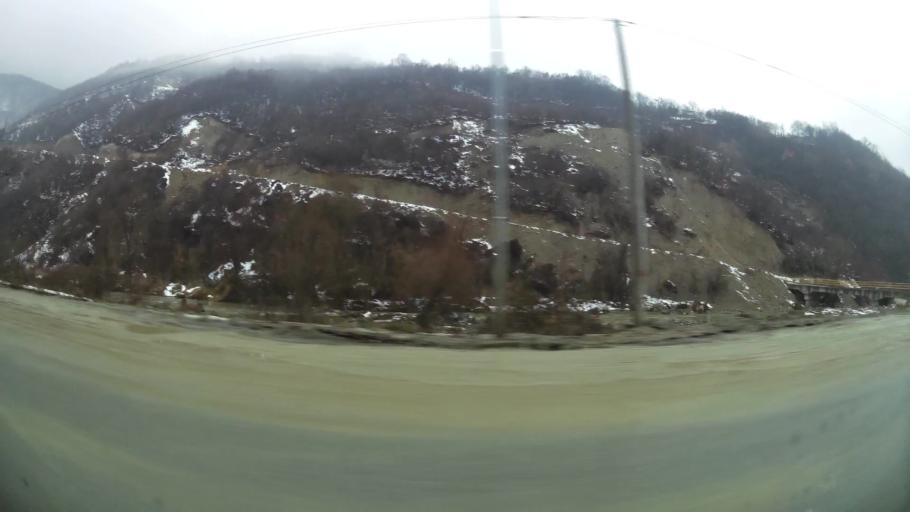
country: XK
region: Ferizaj
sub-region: Hani i Elezit
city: Hani i Elezit
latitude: 42.1656
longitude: 21.2769
